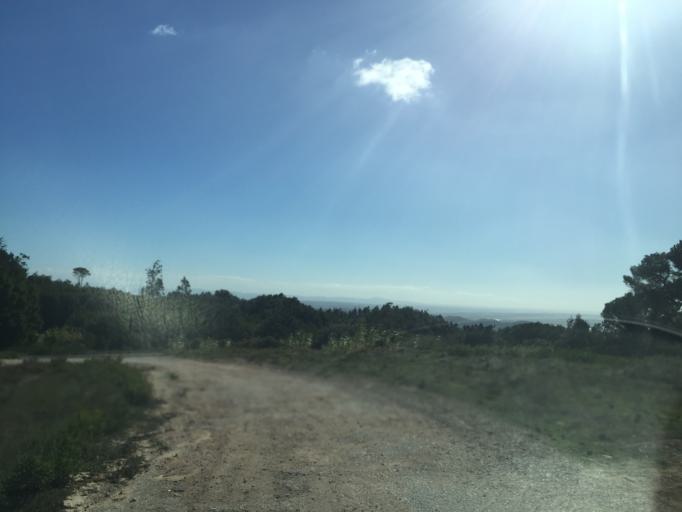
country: PT
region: Coimbra
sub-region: Figueira da Foz
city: Tavarede
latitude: 40.1958
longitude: -8.8542
